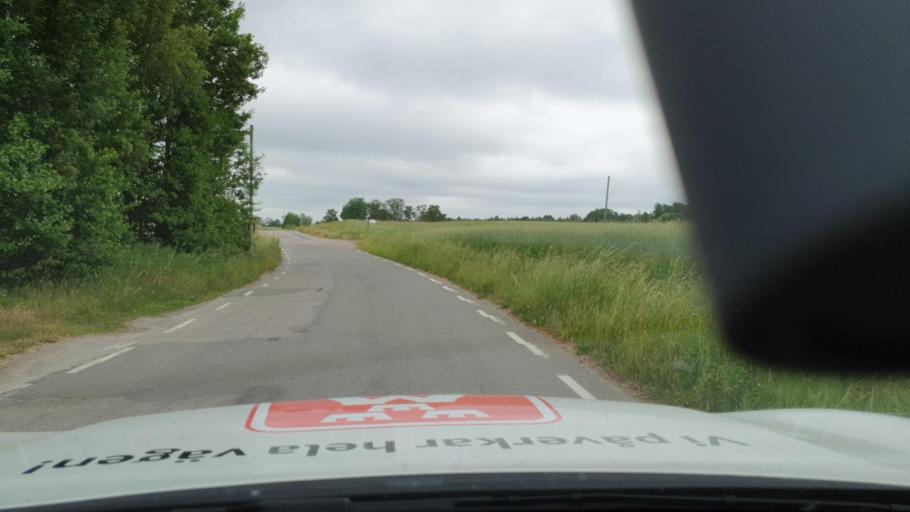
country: SE
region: Vaestra Goetaland
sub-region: Tibro Kommun
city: Tibro
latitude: 58.3775
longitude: 14.1774
